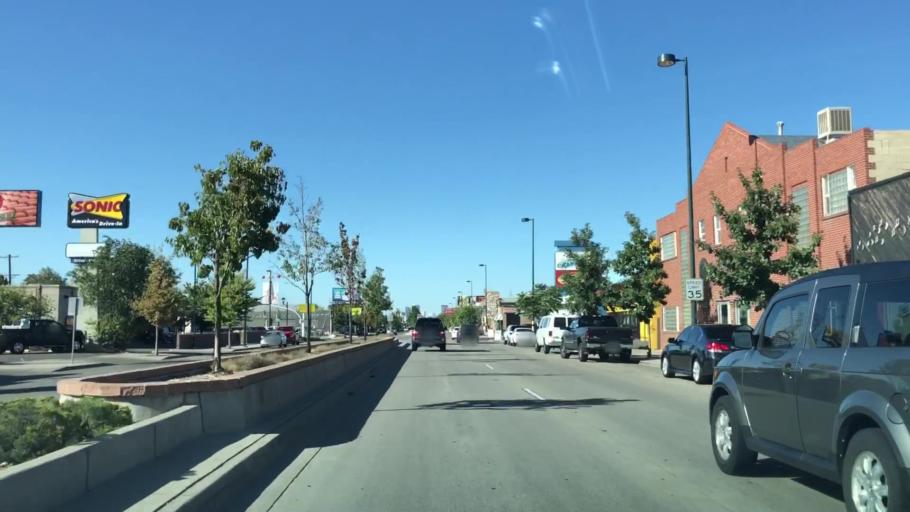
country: US
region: Colorado
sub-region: Arapahoe County
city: Englewood
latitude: 39.6684
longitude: -104.9876
